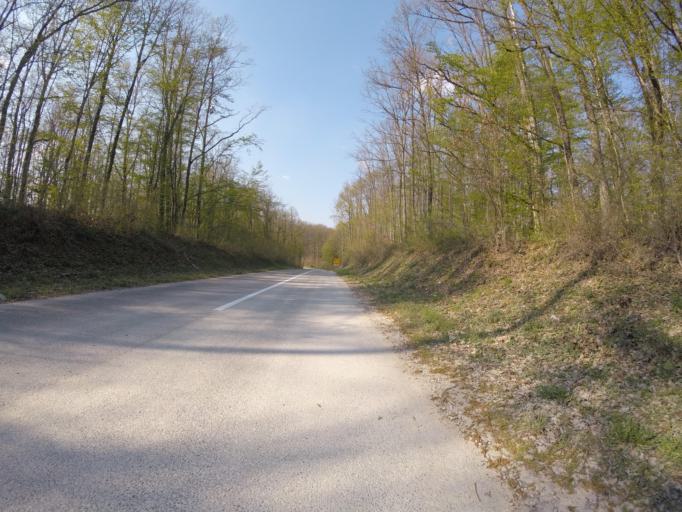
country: HR
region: Sisacko-Moslavacka
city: Glina
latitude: 45.4857
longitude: 16.0471
